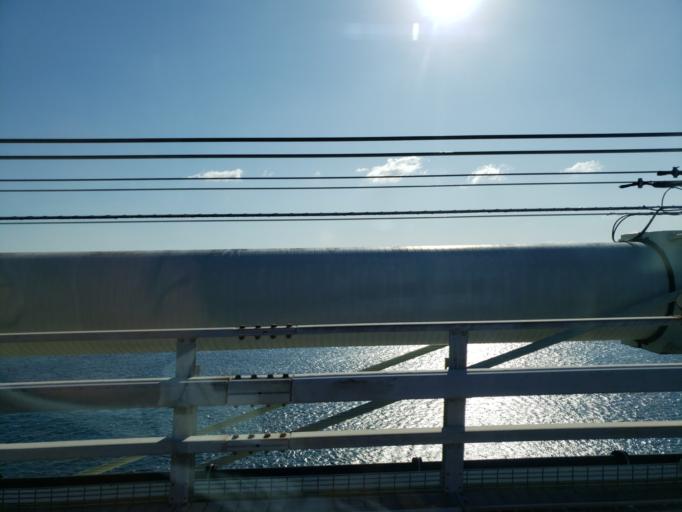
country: JP
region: Hyogo
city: Akashi
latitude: 34.6167
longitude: 135.0211
